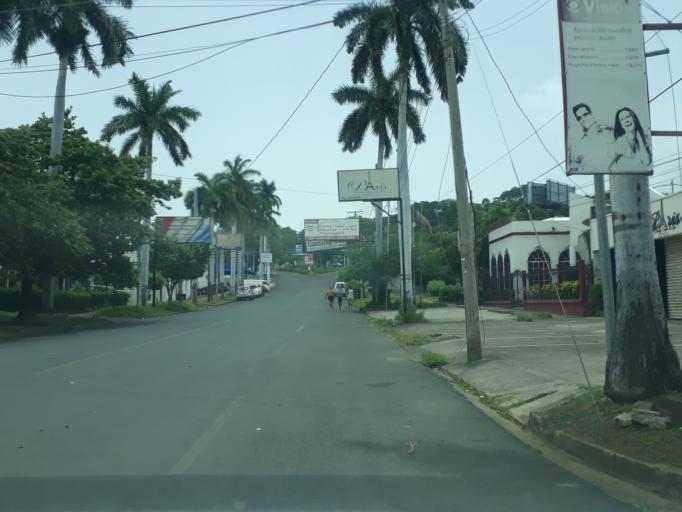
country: NI
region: Managua
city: Managua
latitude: 12.1372
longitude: -86.2769
